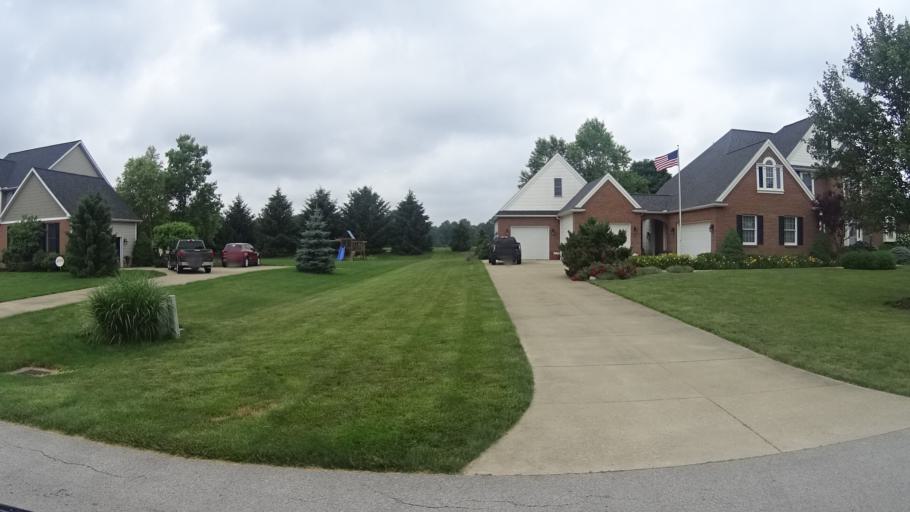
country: US
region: Ohio
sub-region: Erie County
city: Milan
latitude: 41.2956
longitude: -82.5837
